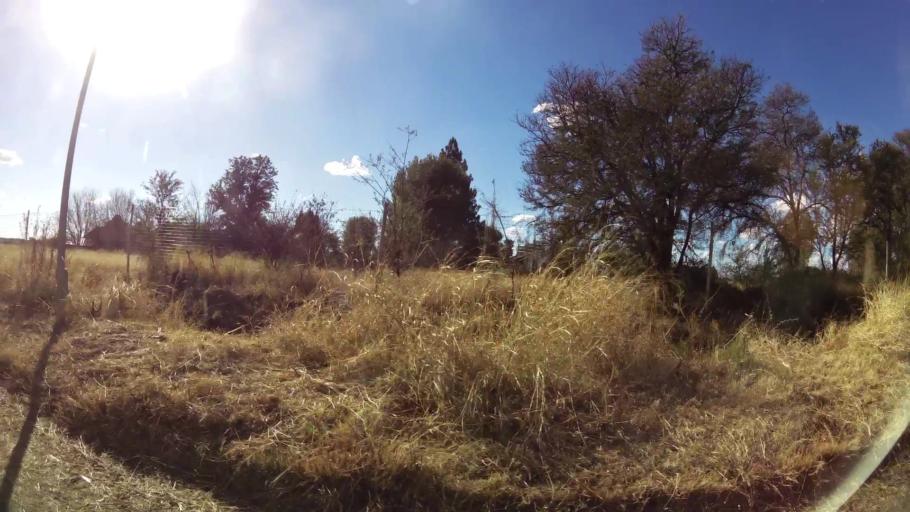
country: ZA
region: North-West
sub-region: Dr Kenneth Kaunda District Municipality
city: Klerksdorp
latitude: -26.8182
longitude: 26.6645
